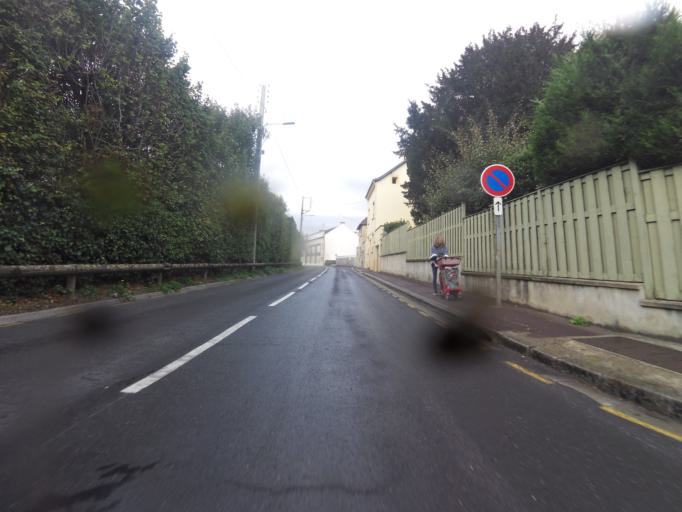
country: FR
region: Lower Normandy
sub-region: Departement du Calvados
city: Caen
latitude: 49.1908
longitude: -0.3698
